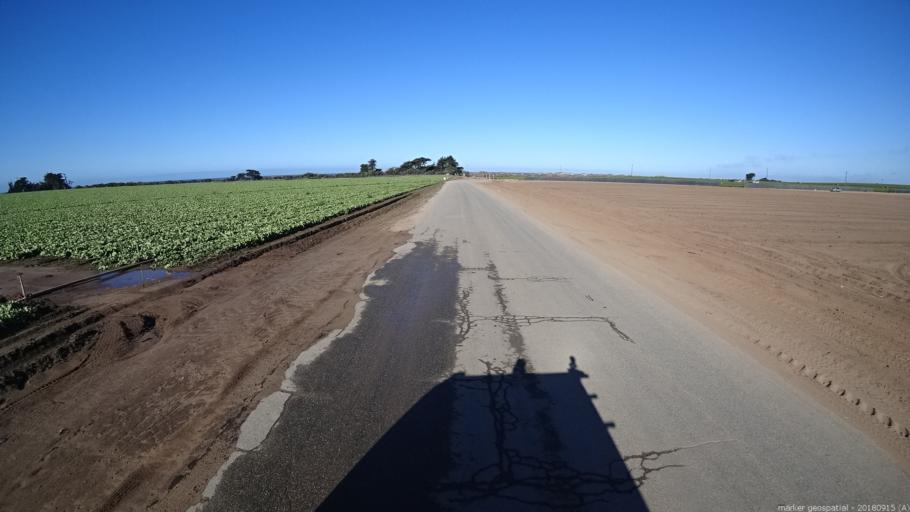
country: US
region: California
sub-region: Monterey County
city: Elkhorn
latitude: 36.8286
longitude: -121.7925
